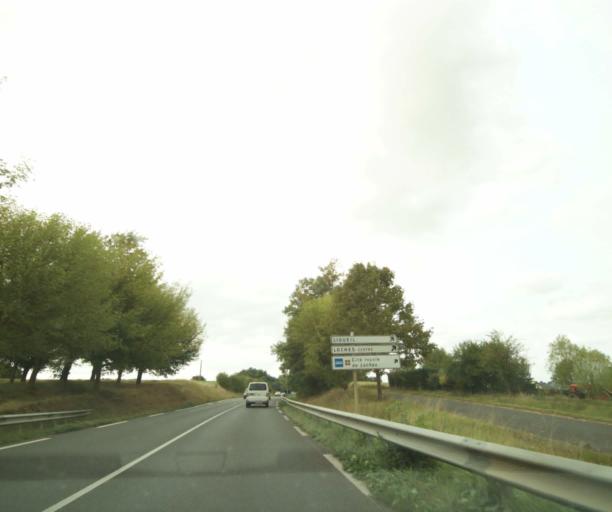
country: FR
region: Centre
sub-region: Departement d'Indre-et-Loire
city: Loches
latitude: 47.1108
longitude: 0.9833
